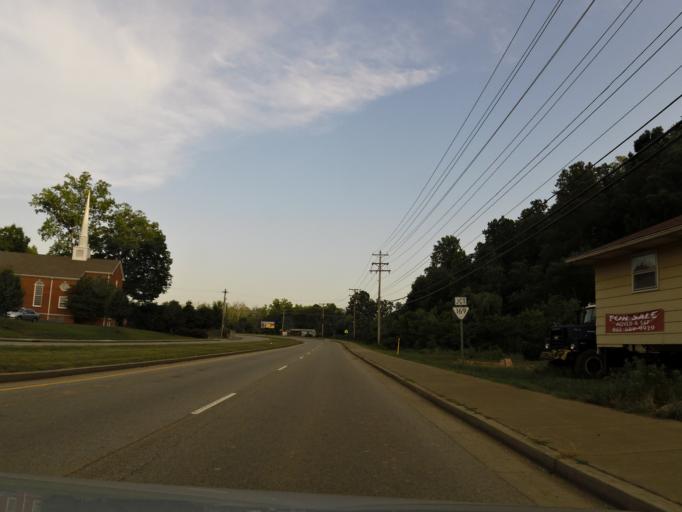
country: US
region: Tennessee
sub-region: Knox County
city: Farragut
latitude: 35.9554
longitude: -84.1256
